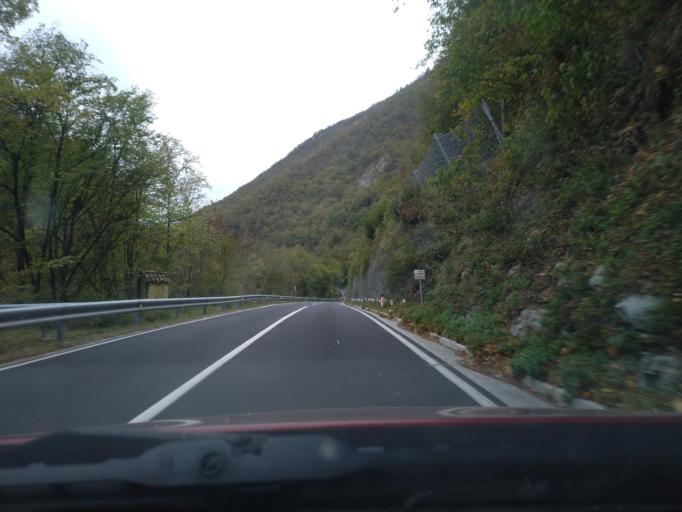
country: SI
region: Tolmin
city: Tolmin
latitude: 46.1256
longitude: 13.7021
